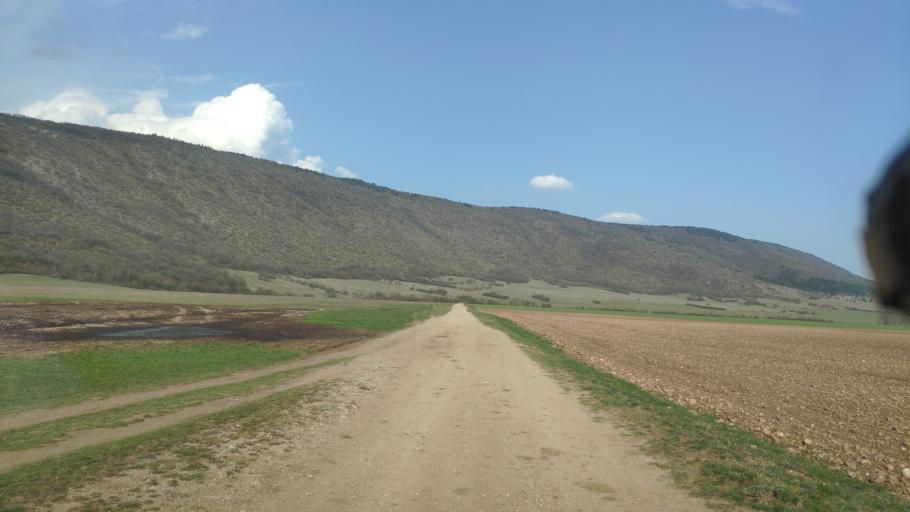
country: SK
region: Kosicky
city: Medzev
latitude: 48.6177
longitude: 20.8835
